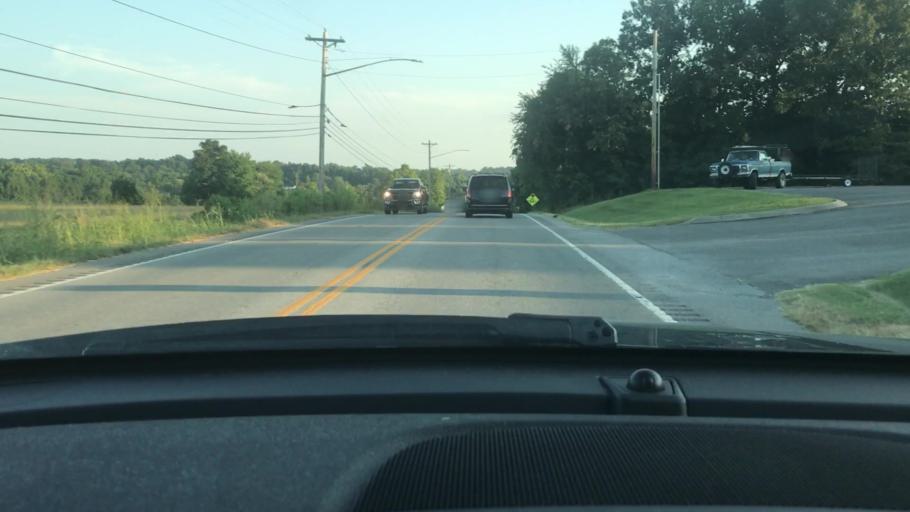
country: US
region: Tennessee
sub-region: Dickson County
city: Dickson
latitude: 36.0931
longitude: -87.3762
